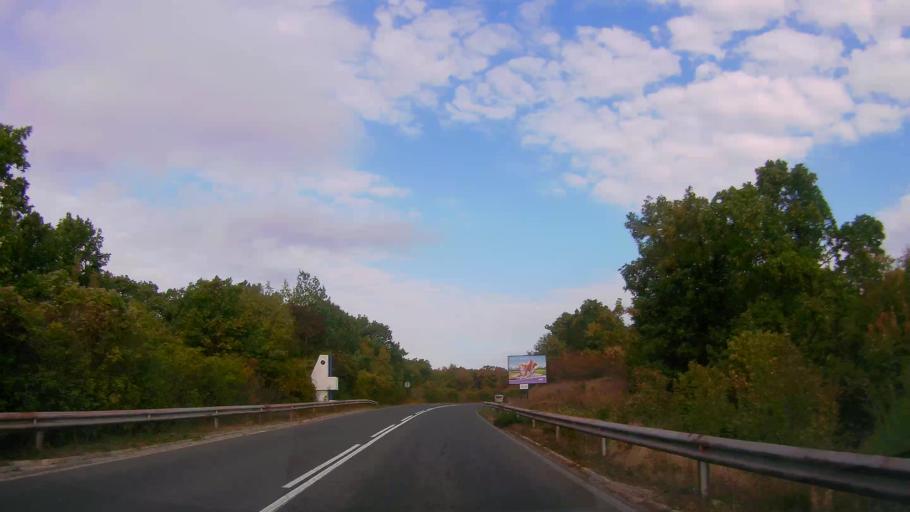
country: BG
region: Burgas
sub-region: Obshtina Sozopol
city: Sozopol
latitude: 42.3360
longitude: 27.7201
